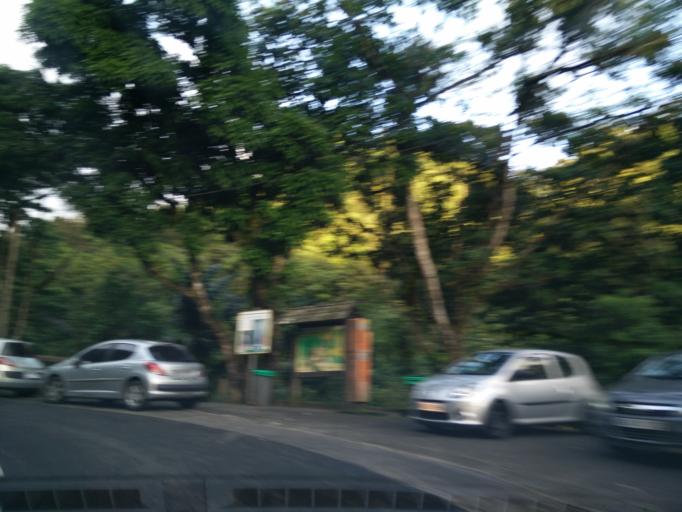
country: MQ
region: Martinique
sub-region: Martinique
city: Le Morne-Rouge
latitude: 14.7251
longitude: -61.1057
